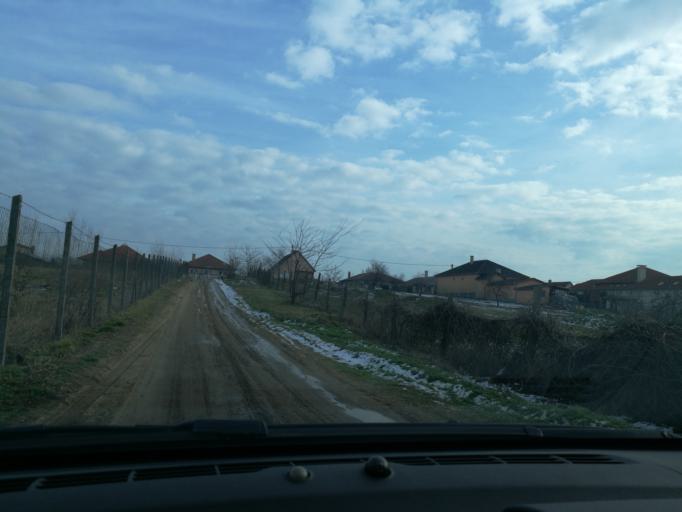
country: HU
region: Szabolcs-Szatmar-Bereg
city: Nyiregyhaza
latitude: 47.9294
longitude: 21.7326
